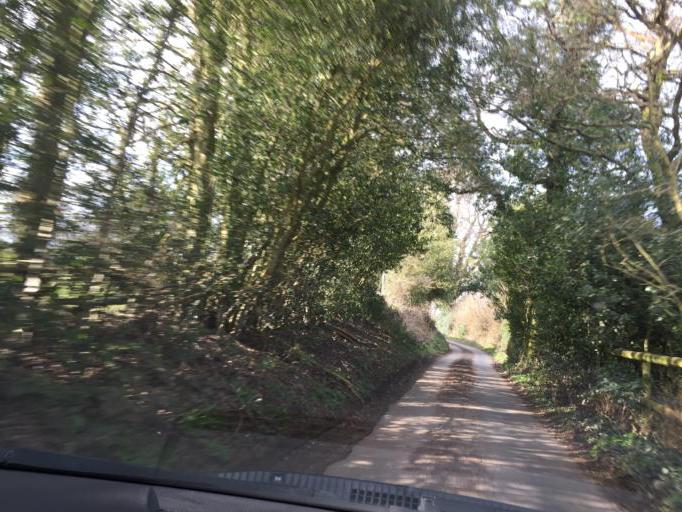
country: GB
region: England
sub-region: Solihull
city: Meriden
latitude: 52.4458
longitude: -1.5931
